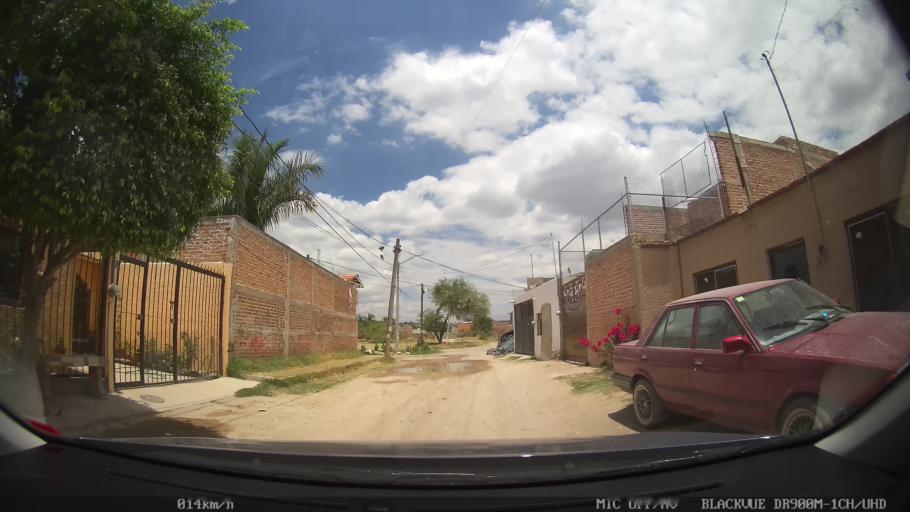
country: MX
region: Jalisco
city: Tlaquepaque
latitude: 20.6404
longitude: -103.2662
